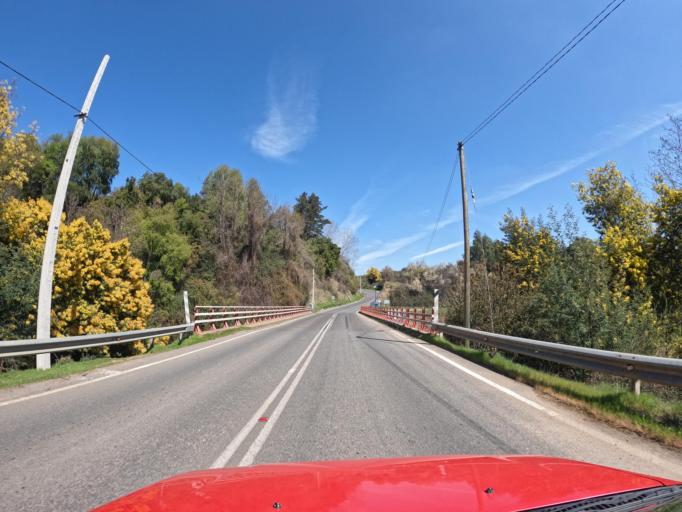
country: CL
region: Maule
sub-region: Provincia de Talca
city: San Clemente
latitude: -35.4688
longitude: -71.2753
